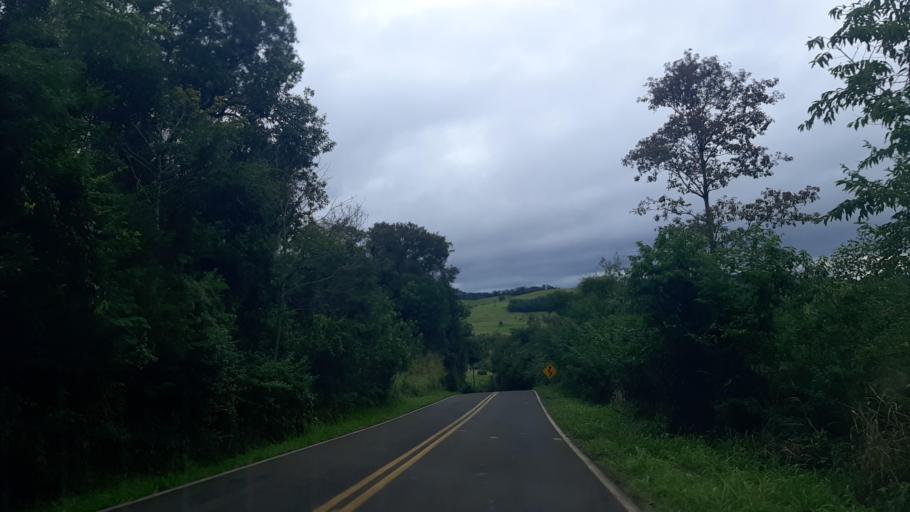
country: BR
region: Parana
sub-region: Ampere
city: Ampere
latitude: -25.9938
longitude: -53.4387
